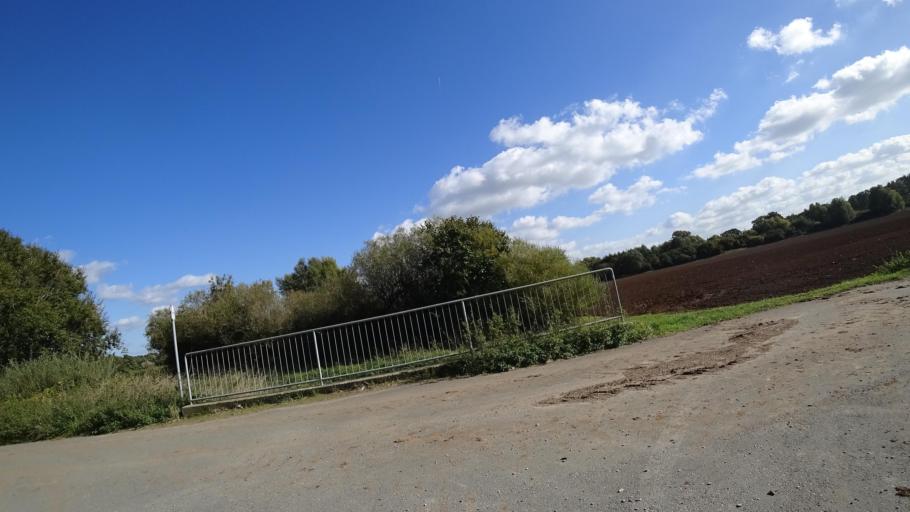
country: DE
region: North Rhine-Westphalia
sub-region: Regierungsbezirk Detmold
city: Rheda-Wiedenbruck
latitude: 51.8635
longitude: 8.2992
